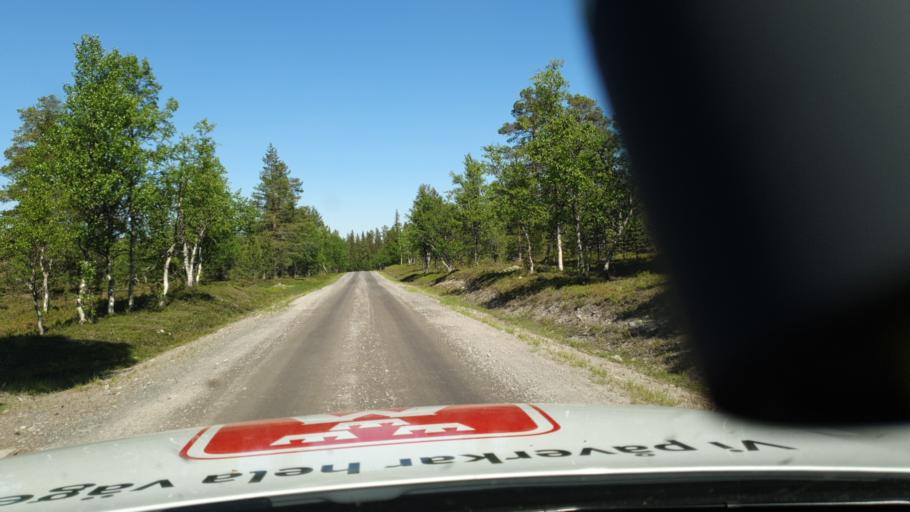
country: NO
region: Hedmark
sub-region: Engerdal
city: Engerdal
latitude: 62.1404
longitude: 12.9417
